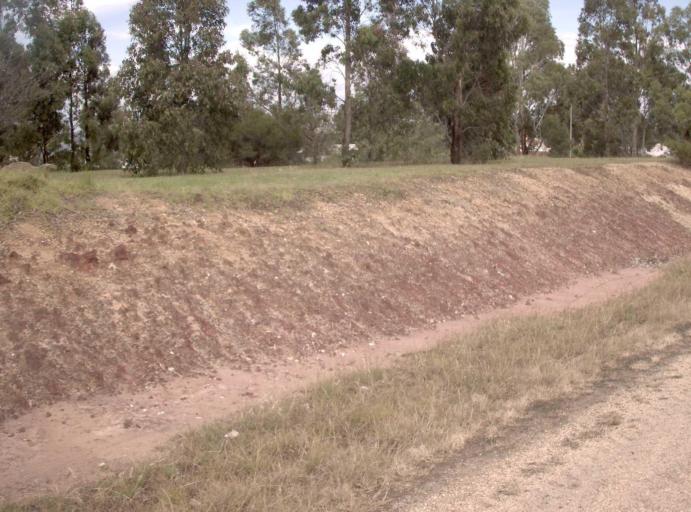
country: AU
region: Victoria
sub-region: Wellington
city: Sale
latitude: -37.9718
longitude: 146.9865
